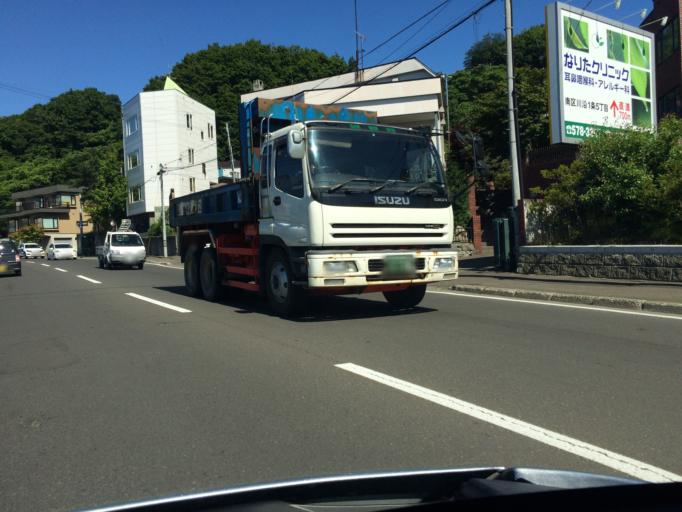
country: JP
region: Hokkaido
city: Sapporo
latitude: 43.0004
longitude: 141.3339
